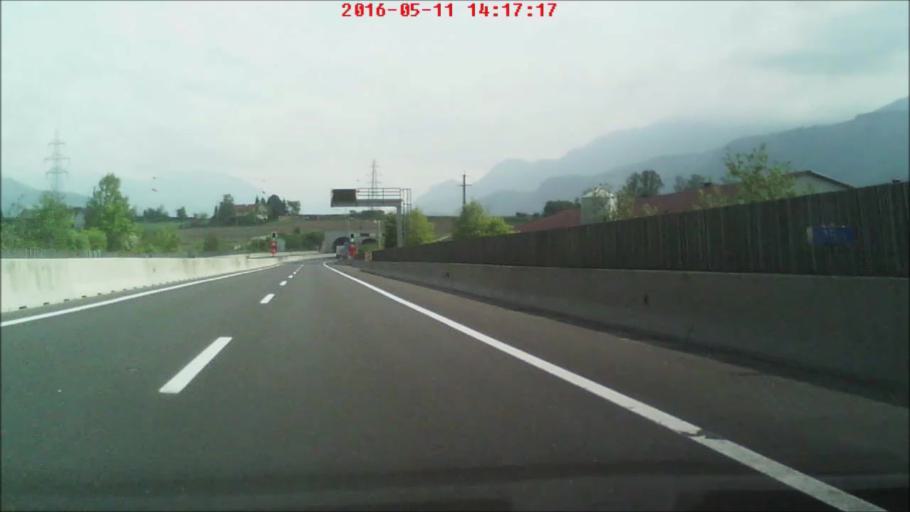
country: AT
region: Upper Austria
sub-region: Politischer Bezirk Kirchdorf an der Krems
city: Micheldorf in Oberoesterreich
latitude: 47.9269
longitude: 14.0986
